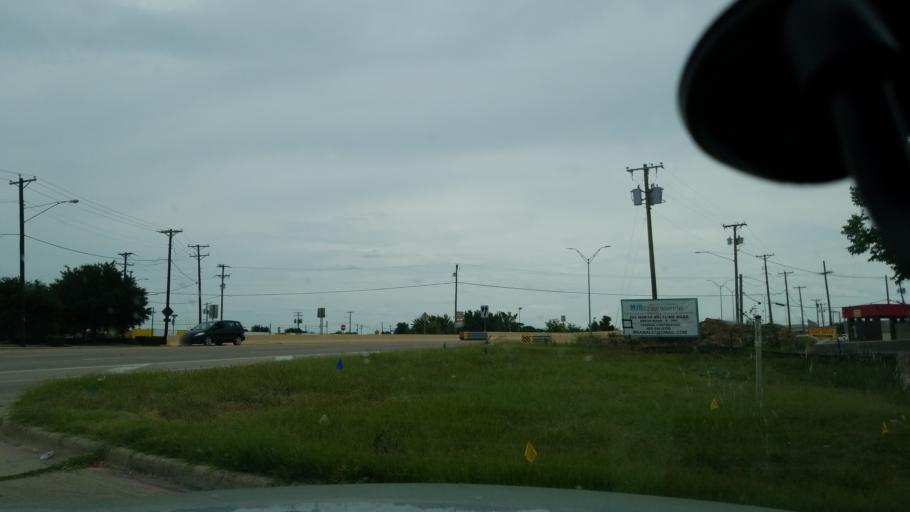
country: US
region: Texas
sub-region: Dallas County
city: Grand Prairie
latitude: 32.7483
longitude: -96.9949
